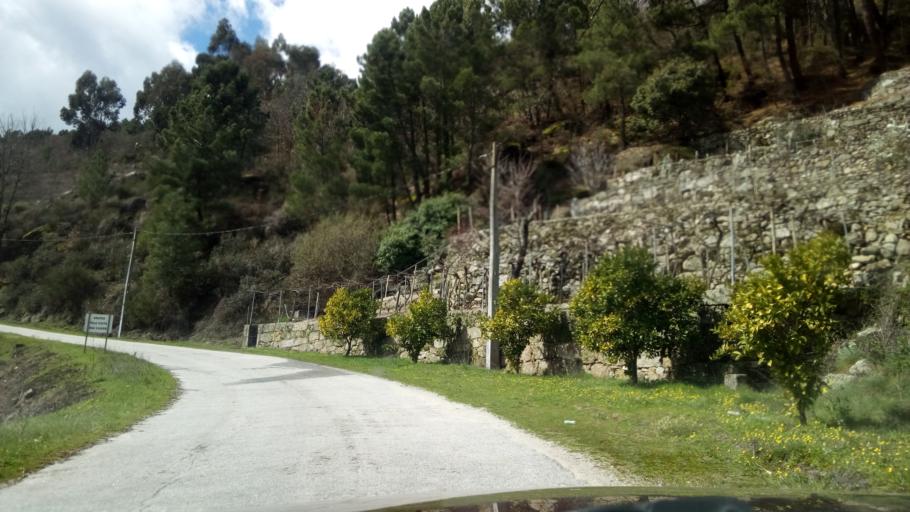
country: PT
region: Guarda
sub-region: Fornos de Algodres
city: Fornos de Algodres
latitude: 40.6622
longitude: -7.4987
